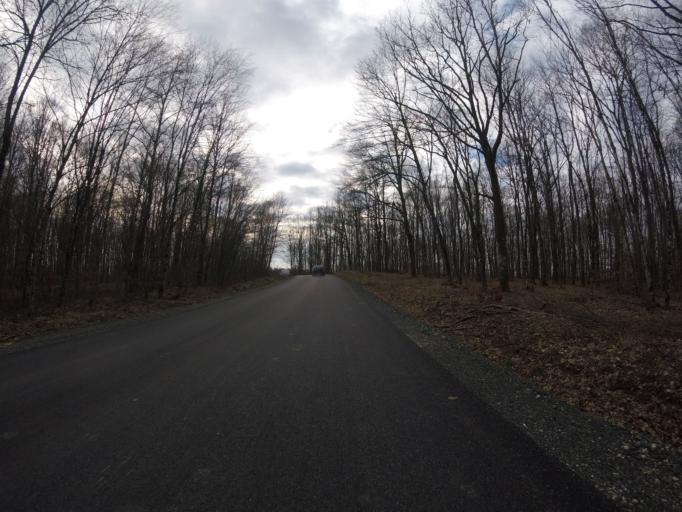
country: HR
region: Sisacko-Moslavacka
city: Glina
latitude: 45.4897
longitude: 16.0452
